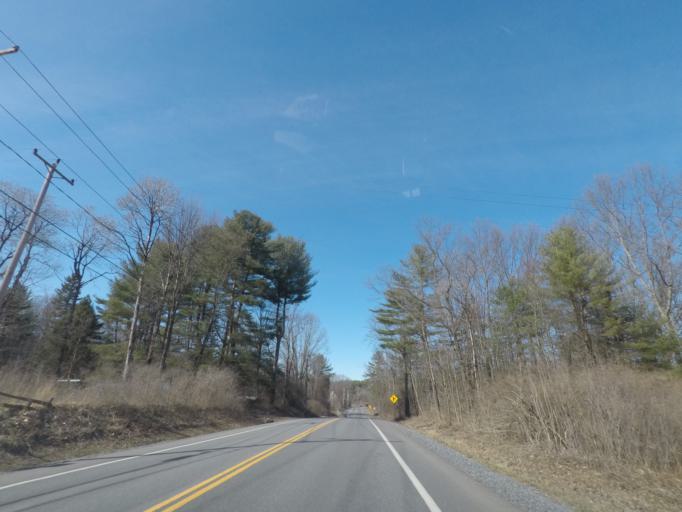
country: US
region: New York
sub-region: Saratoga County
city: Milton
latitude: 43.0635
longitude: -73.8502
